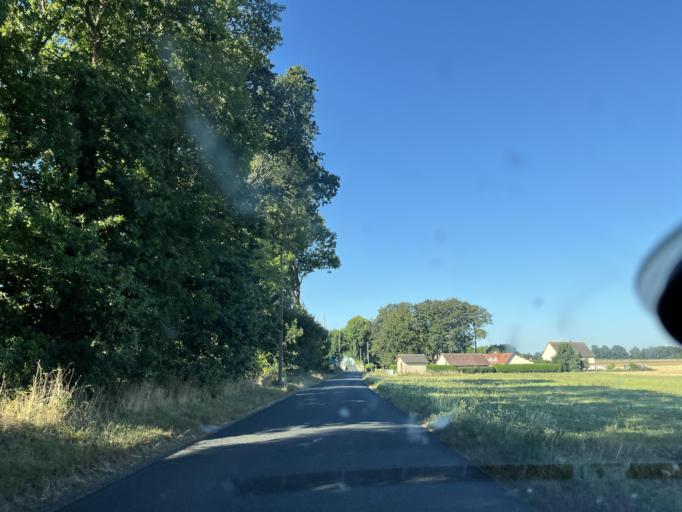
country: FR
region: Haute-Normandie
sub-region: Departement de la Seine-Maritime
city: Lillebonne
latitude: 49.5599
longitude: 0.5809
